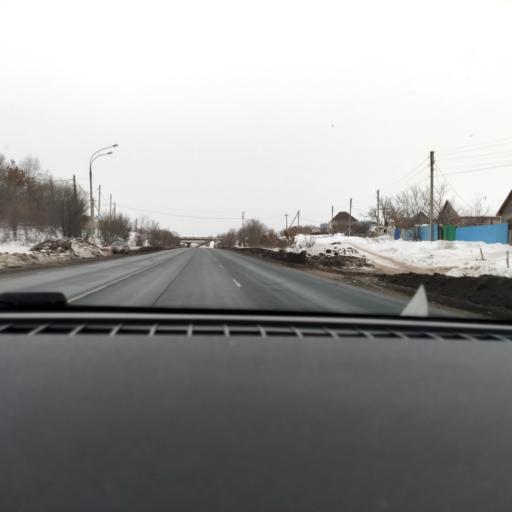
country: RU
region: Samara
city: Smyshlyayevka
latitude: 53.2373
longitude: 50.4845
